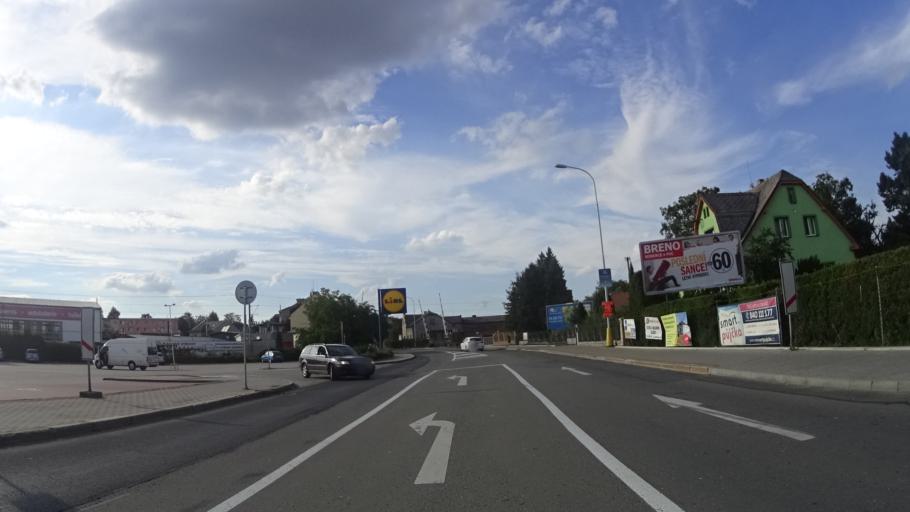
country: CZ
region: Olomoucky
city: Zabreh
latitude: 49.8778
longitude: 16.8838
